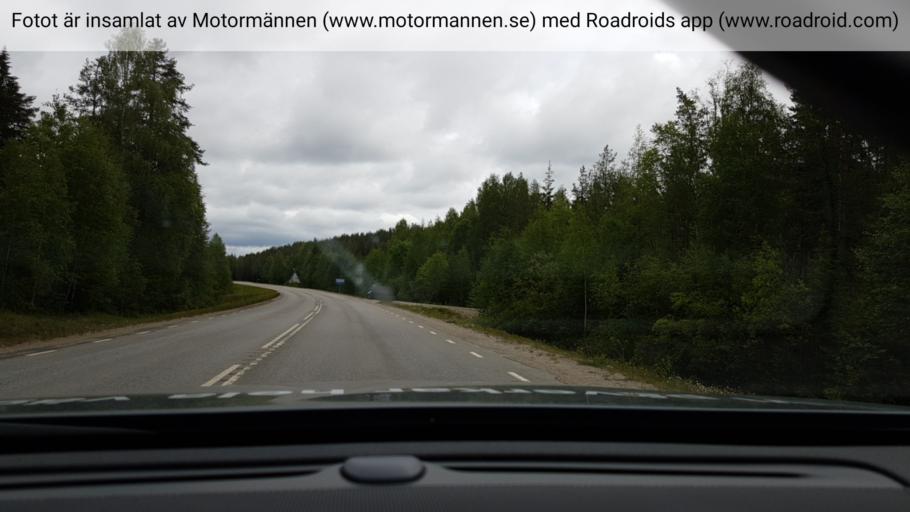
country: SE
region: Vaesterbotten
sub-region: Lycksele Kommun
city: Lycksele
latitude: 64.5767
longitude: 18.6540
